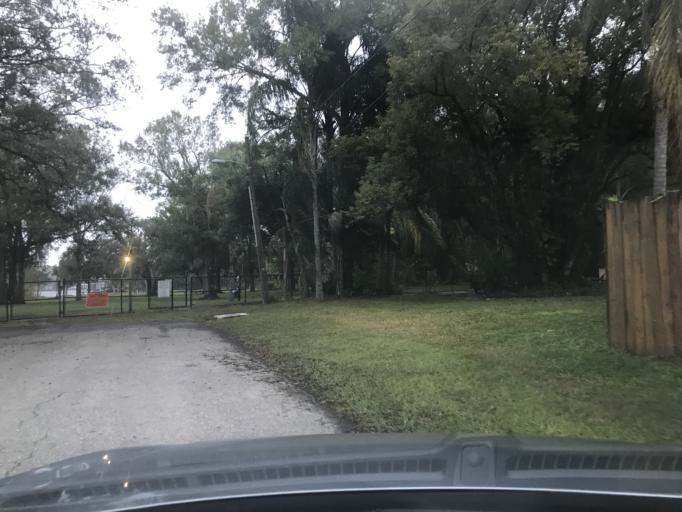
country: US
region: Florida
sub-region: Hillsborough County
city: Tampa
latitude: 27.9847
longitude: -82.4712
